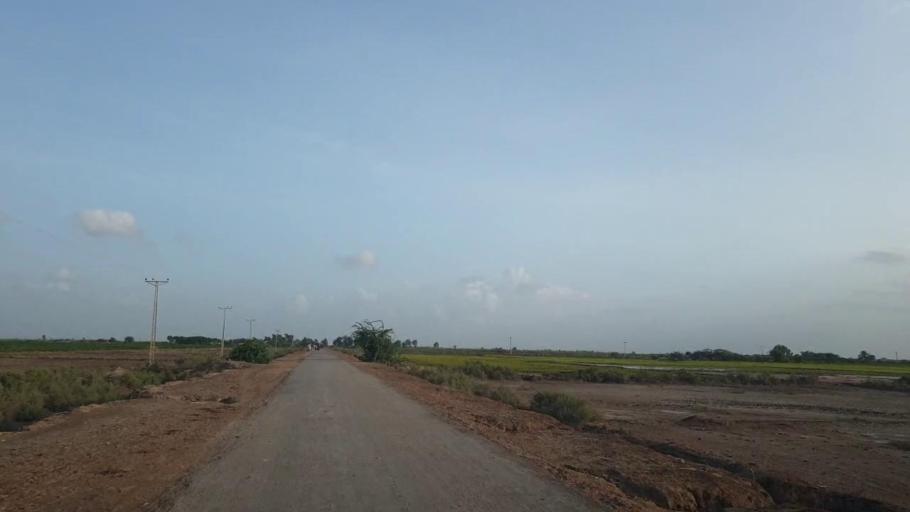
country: PK
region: Sindh
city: Kadhan
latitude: 24.6227
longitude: 69.1158
